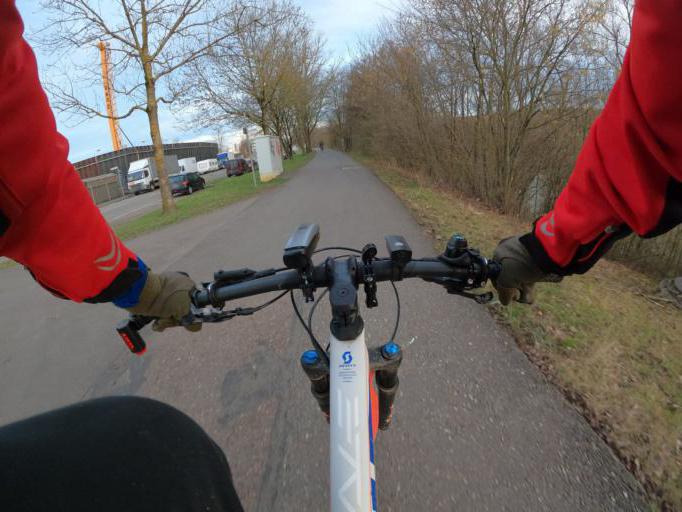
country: DE
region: Baden-Wuerttemberg
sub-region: Regierungsbezirk Stuttgart
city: Denkendorf
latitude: 48.7234
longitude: 9.3392
